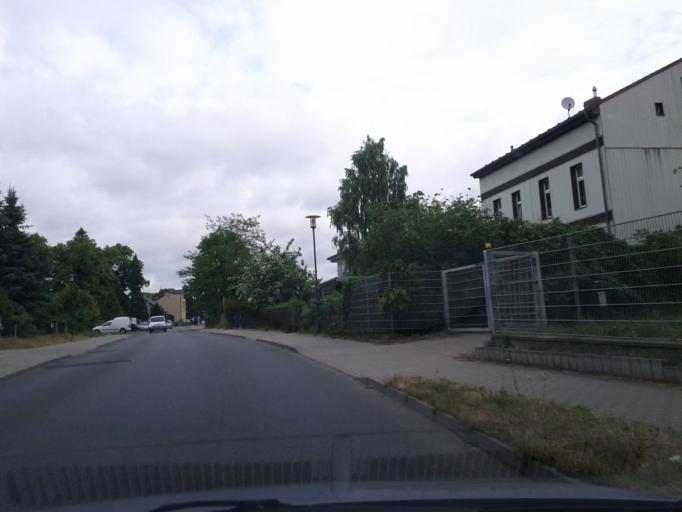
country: DE
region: Brandenburg
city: Woltersdorf
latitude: 52.4473
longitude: 13.7557
